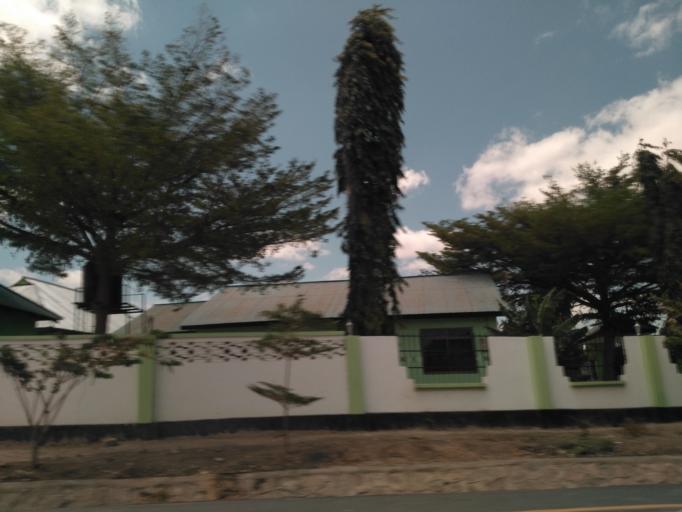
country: TZ
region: Dodoma
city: Kisasa
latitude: -6.1696
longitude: 35.7978
